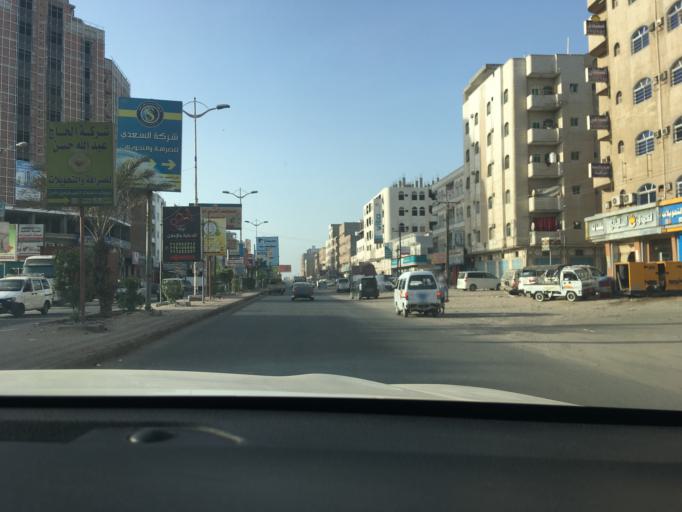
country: YE
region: Aden
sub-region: Al Mansura
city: Al Mansurah
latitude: 12.8616
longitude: 44.9721
